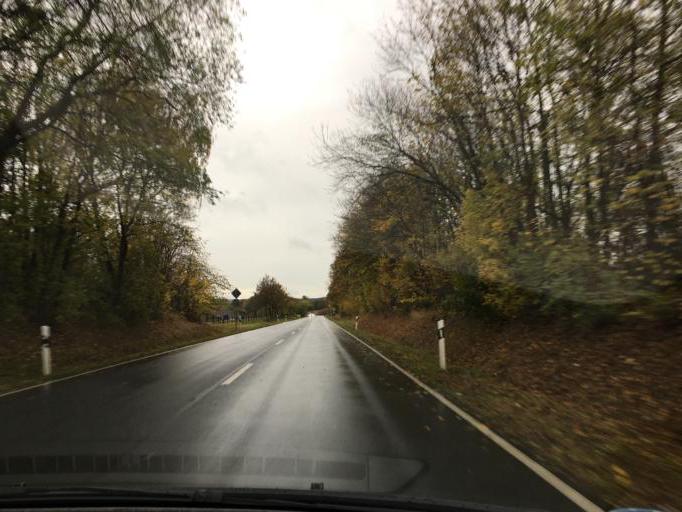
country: DE
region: North Rhine-Westphalia
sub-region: Regierungsbezirk Koln
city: Nideggen
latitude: 50.6506
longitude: 6.5436
